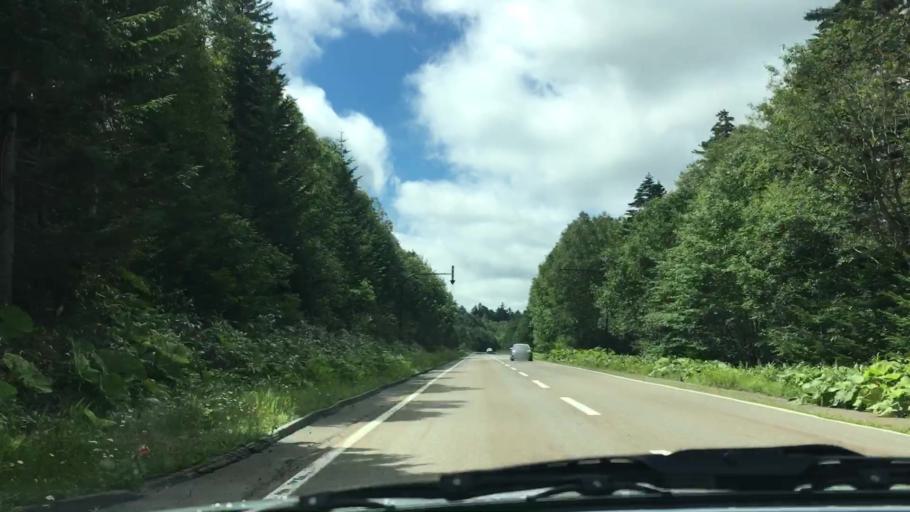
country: JP
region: Hokkaido
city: Kitami
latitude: 43.4324
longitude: 143.9938
